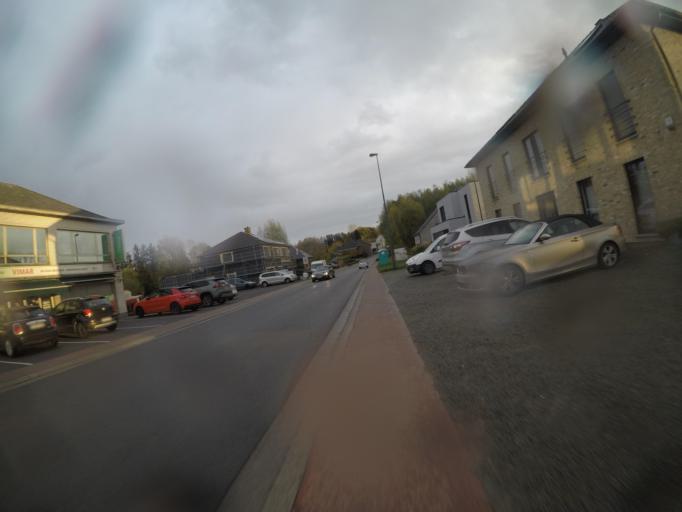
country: BE
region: Flanders
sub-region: Provincie Vlaams-Brabant
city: Ternat
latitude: 50.8519
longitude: 4.1342
